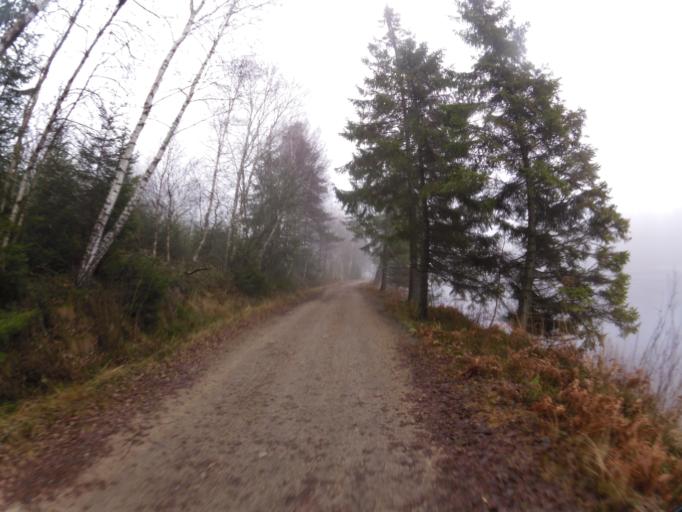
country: NO
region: Ostfold
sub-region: Fredrikstad
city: Fredrikstad
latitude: 59.2502
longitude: 10.9631
